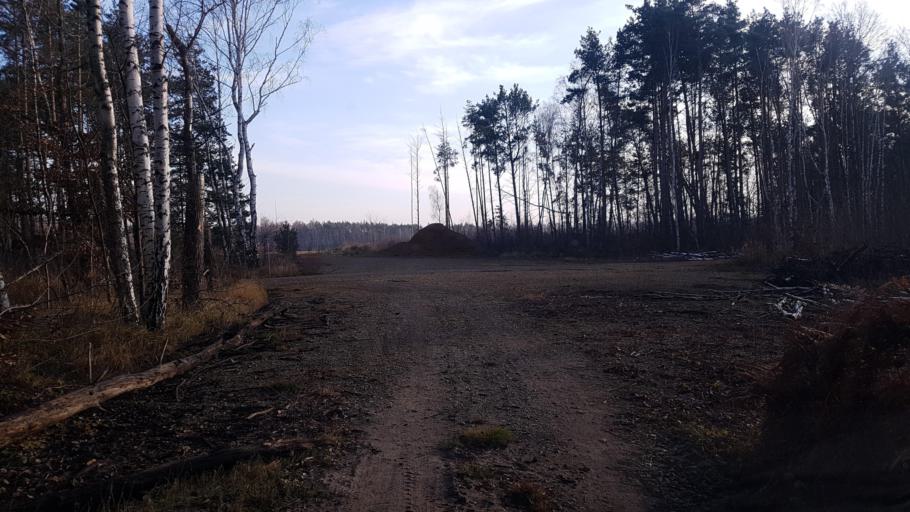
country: DE
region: Brandenburg
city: Plessa
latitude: 51.5225
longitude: 13.6829
